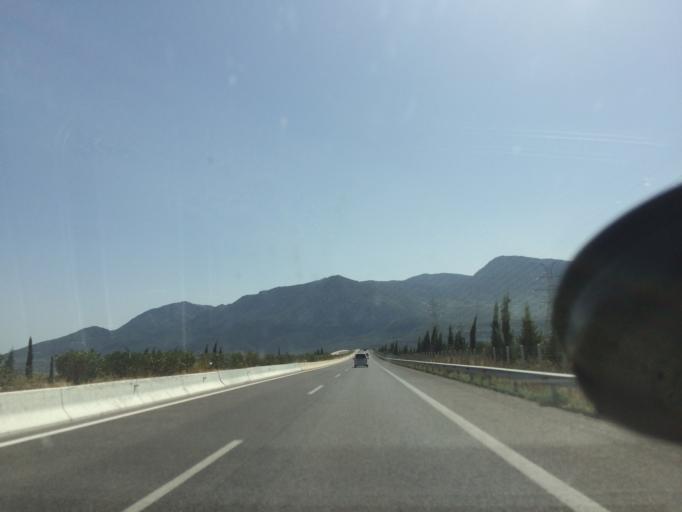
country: GR
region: Central Greece
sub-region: Nomos Fthiotidos
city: Anthili
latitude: 38.8352
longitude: 22.4796
